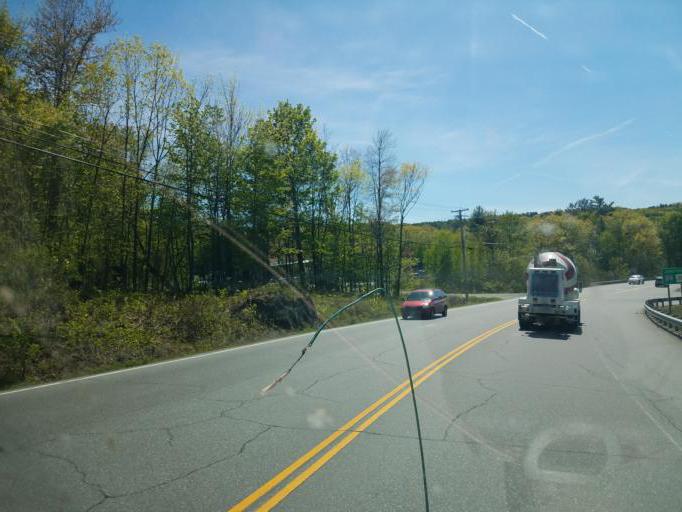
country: US
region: New Hampshire
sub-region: Grafton County
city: Lebanon
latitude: 43.6346
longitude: -72.2061
